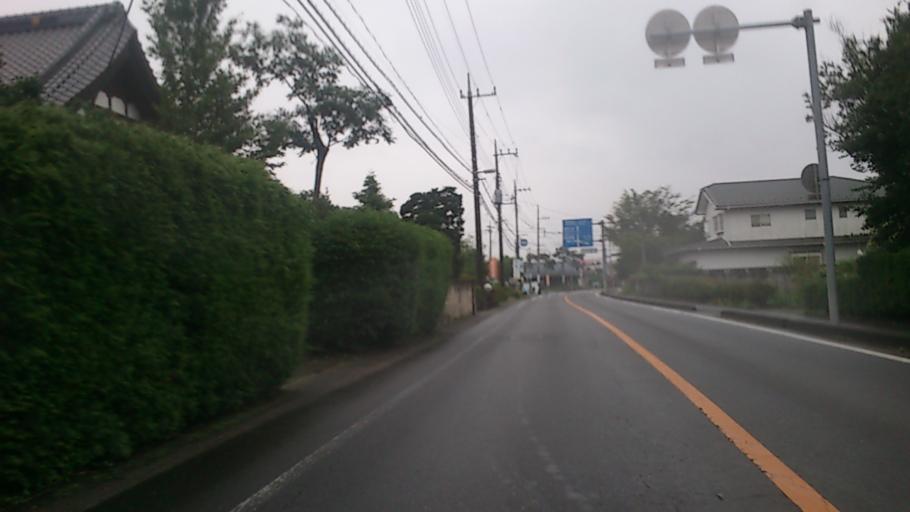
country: JP
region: Tochigi
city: Karasuyama
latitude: 36.7687
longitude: 140.1267
